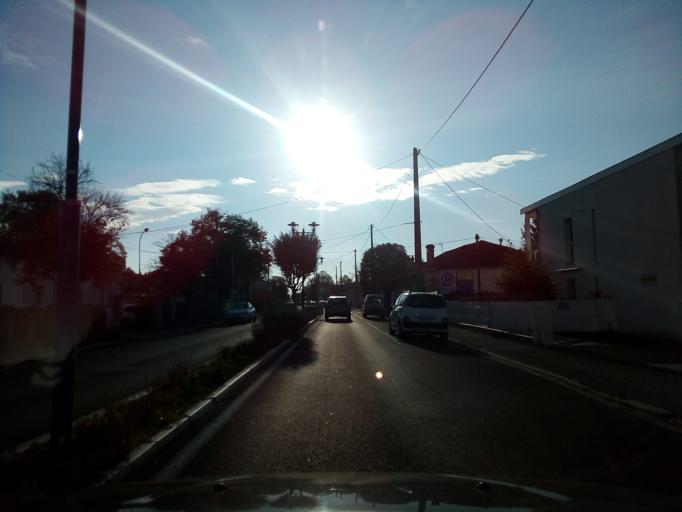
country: FR
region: Aquitaine
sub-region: Departement de la Gironde
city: Andernos-les-Bains
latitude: 44.7450
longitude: -1.0942
